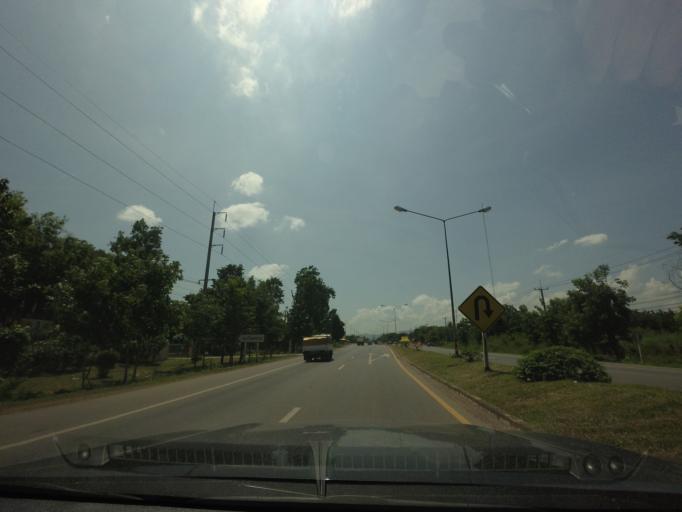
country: TH
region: Phetchabun
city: Lom Sak
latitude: 16.7000
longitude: 101.1723
